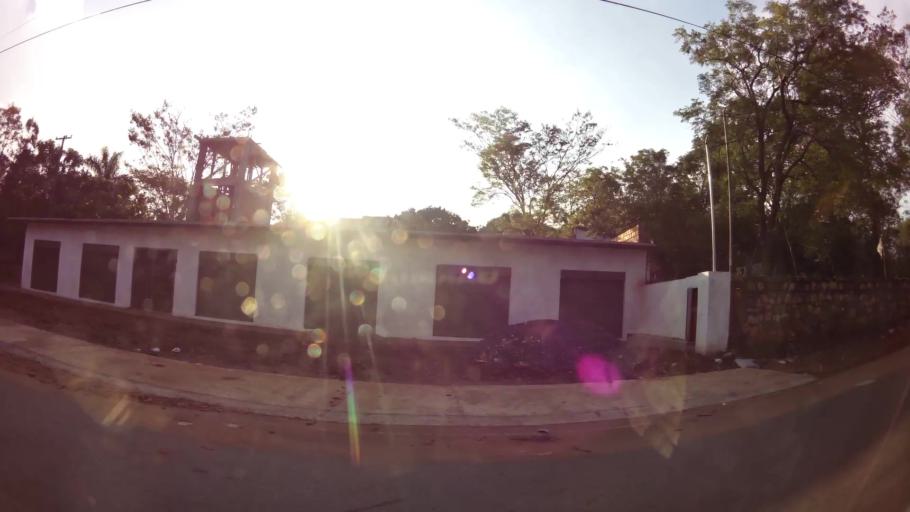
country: PY
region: Central
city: Fernando de la Mora
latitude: -25.3648
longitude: -57.5304
